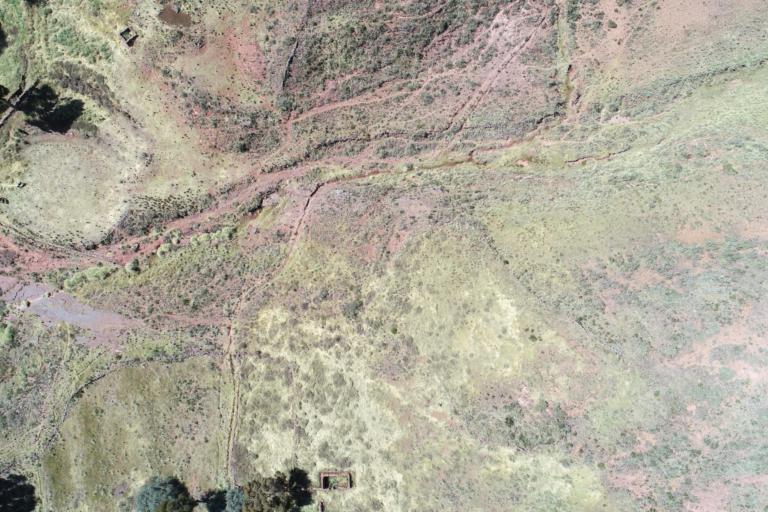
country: BO
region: La Paz
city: Tiahuanaco
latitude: -16.6047
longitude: -68.7732
